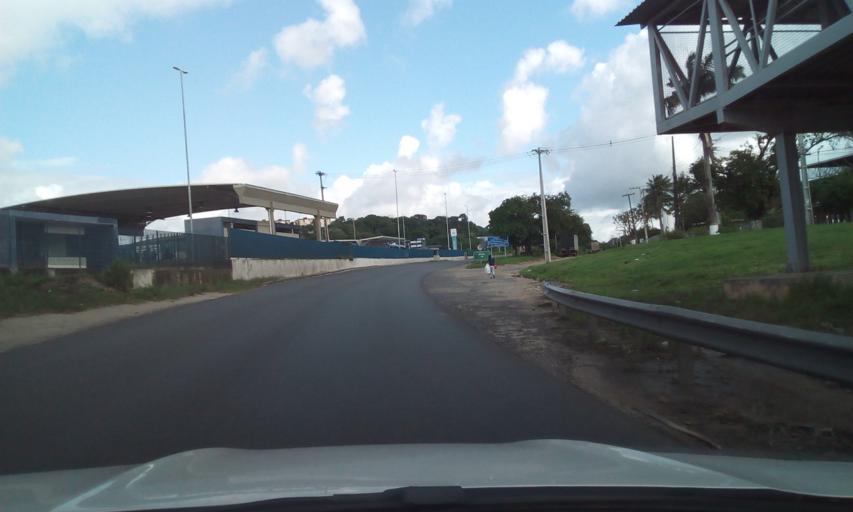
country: BR
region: Pernambuco
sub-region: Abreu E Lima
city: Abreu e Lima
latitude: -7.9202
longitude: -34.8954
